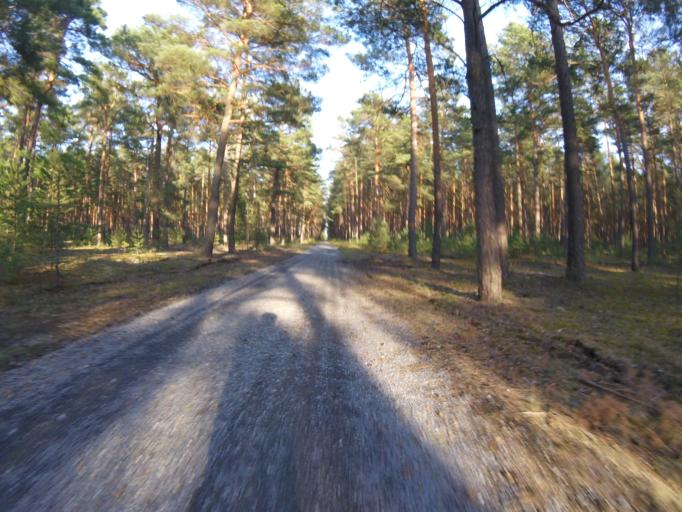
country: DE
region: Brandenburg
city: Gross Koris
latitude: 52.1784
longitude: 13.7166
